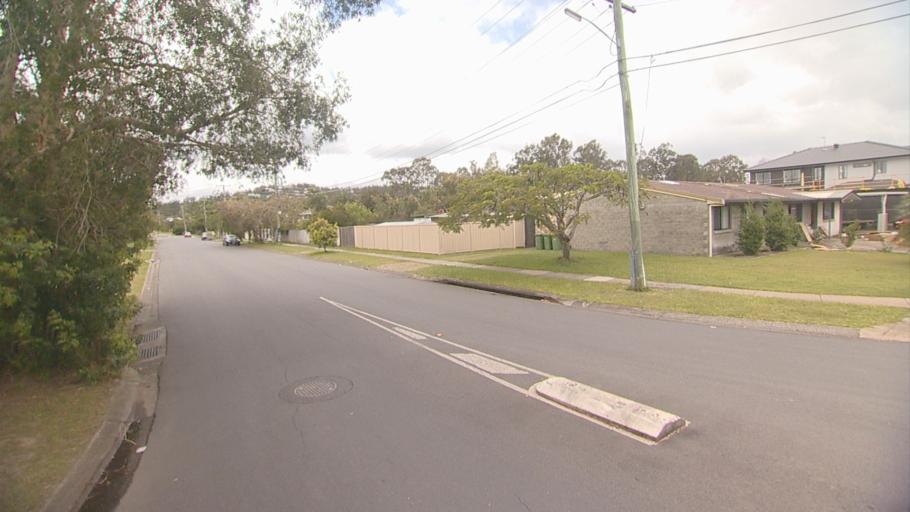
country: AU
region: Queensland
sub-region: Logan
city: Slacks Creek
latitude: -27.6712
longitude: 153.1848
